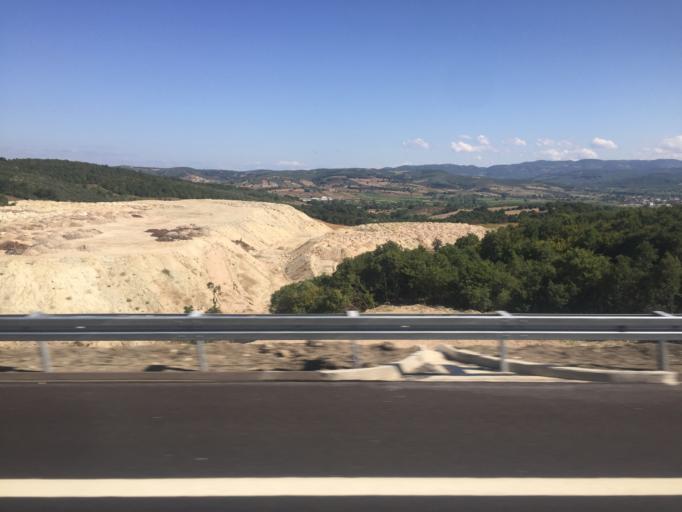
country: TR
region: Bursa
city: Mahmudiye
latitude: 40.2568
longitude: 28.7268
